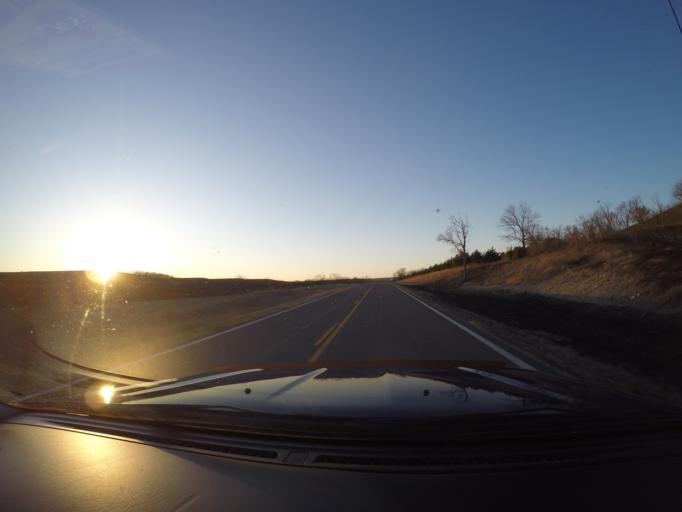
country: US
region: Kansas
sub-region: Wabaunsee County
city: Alma
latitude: 38.8792
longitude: -96.2627
